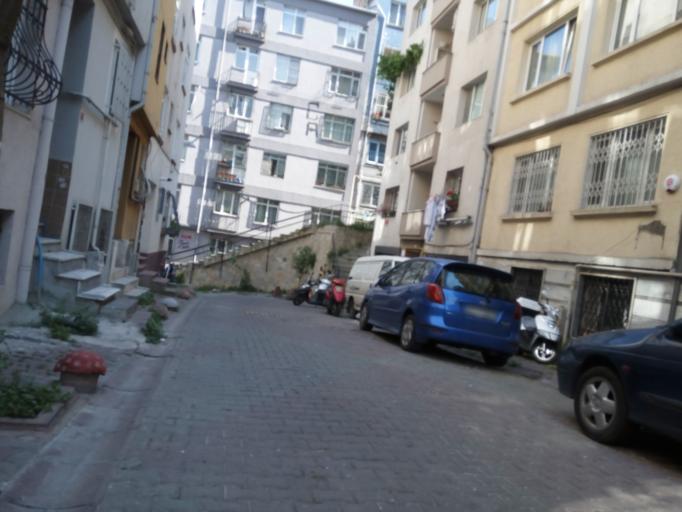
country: TR
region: Istanbul
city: Eminoenue
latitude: 41.0328
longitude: 28.9870
